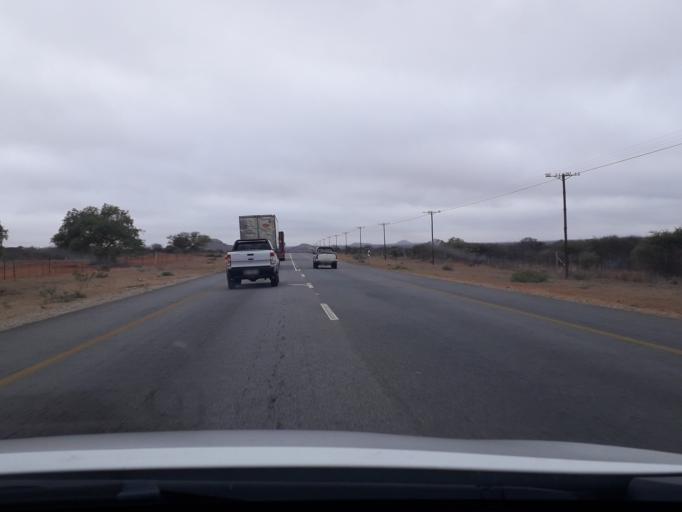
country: ZA
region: Limpopo
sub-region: Capricorn District Municipality
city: Mankoeng
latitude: -23.5623
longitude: 29.6821
